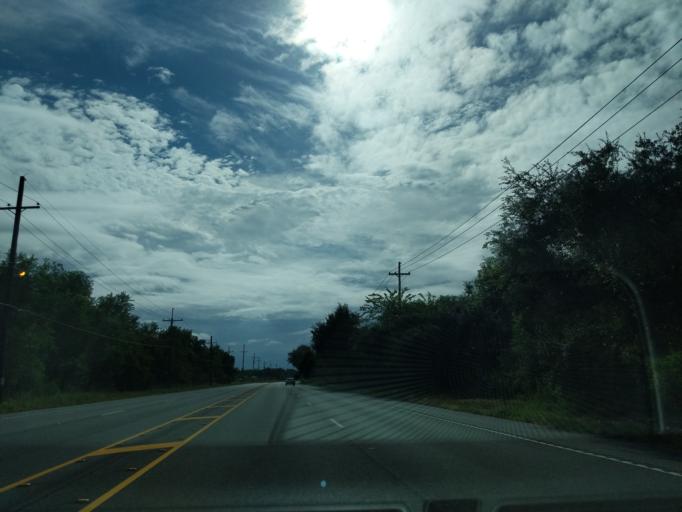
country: US
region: Louisiana
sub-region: Saint Bernard Parish
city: Meraux
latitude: 30.0581
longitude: -89.8710
